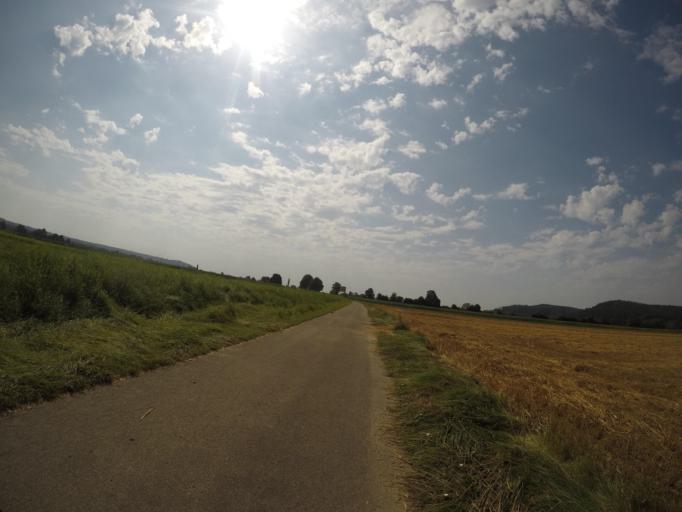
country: DE
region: Baden-Wuerttemberg
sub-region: Tuebingen Region
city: Kirchberg an der Iller
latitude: 48.1564
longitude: 10.0833
